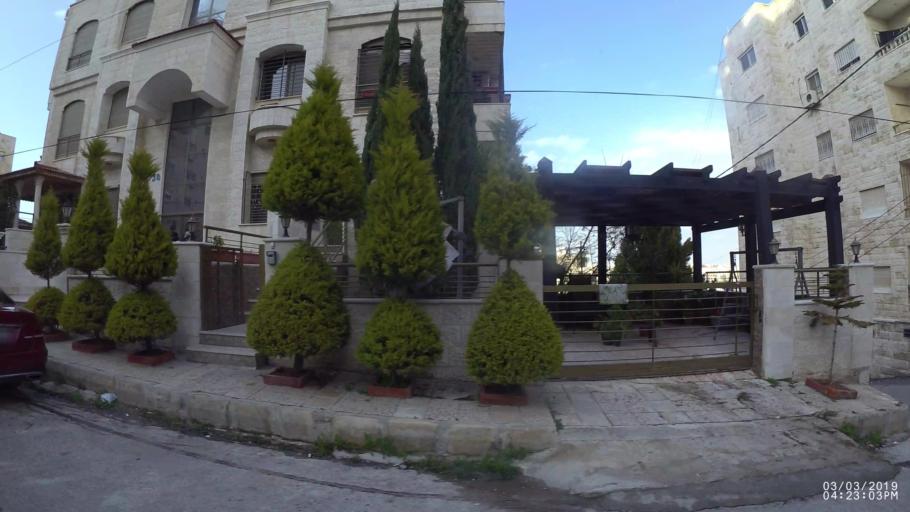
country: JO
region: Amman
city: Al Jubayhah
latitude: 31.9829
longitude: 35.8840
